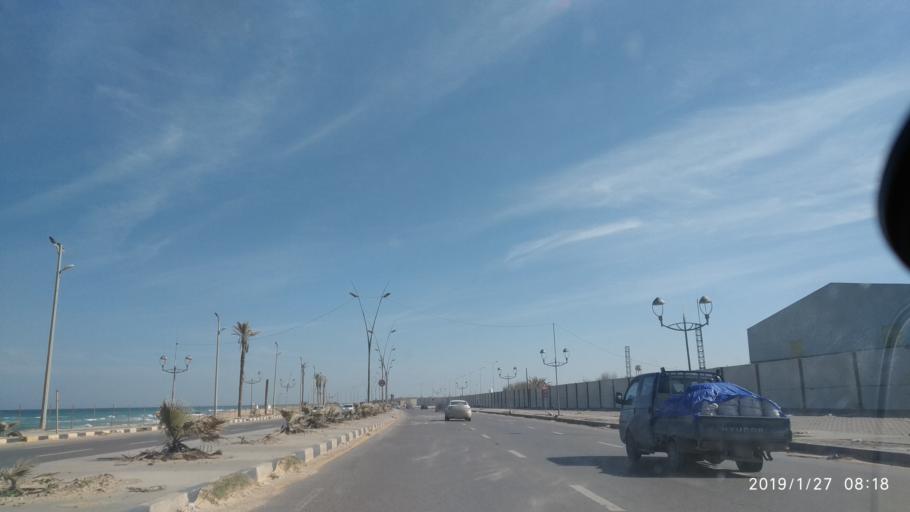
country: LY
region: Tripoli
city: Tagiura
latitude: 32.9084
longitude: 13.2799
